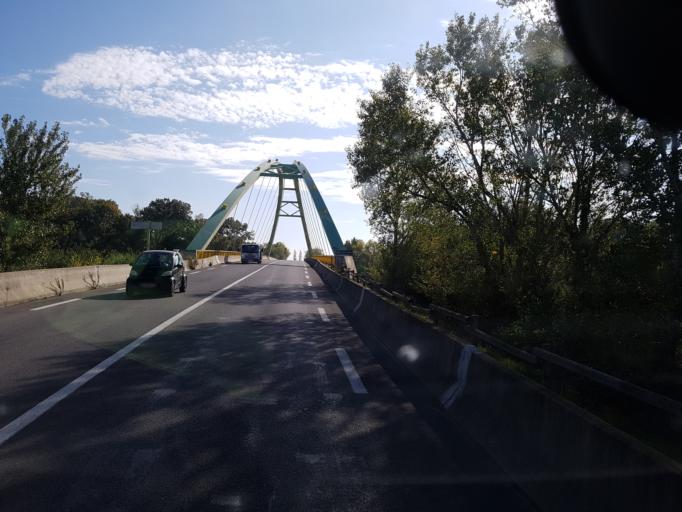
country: FR
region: Languedoc-Roussillon
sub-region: Departement du Gard
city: Saint-Gilles
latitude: 43.6665
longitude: 4.4520
